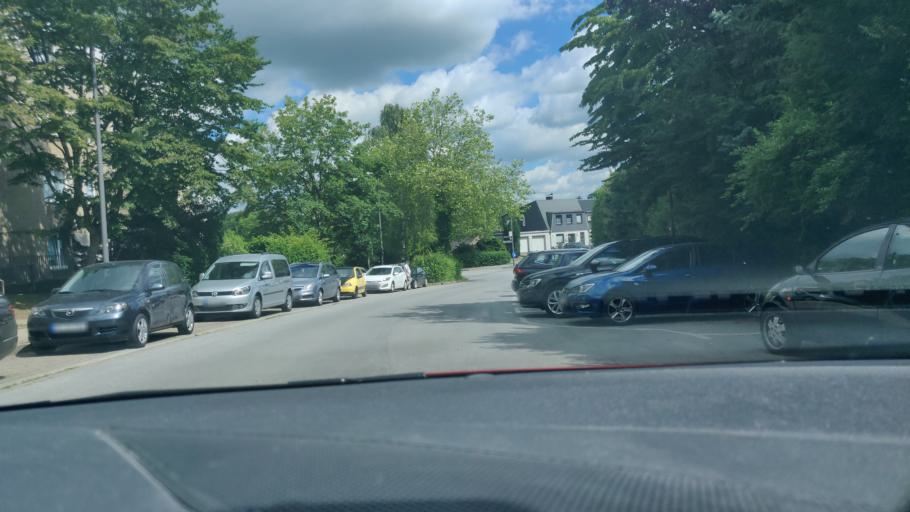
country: DE
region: North Rhine-Westphalia
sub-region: Regierungsbezirk Dusseldorf
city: Heiligenhaus
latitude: 51.3254
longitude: 6.9867
